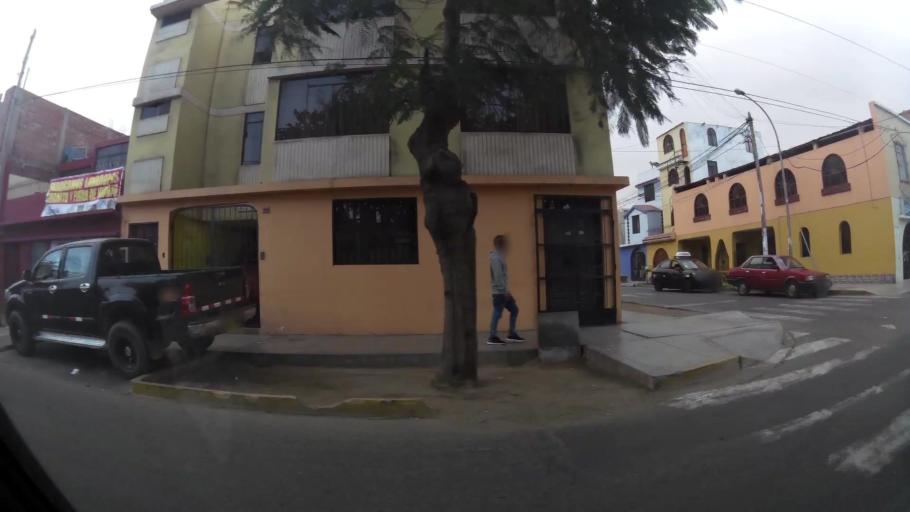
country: PE
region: La Libertad
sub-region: Provincia de Trujillo
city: La Esperanza
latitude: -8.0928
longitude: -79.0356
